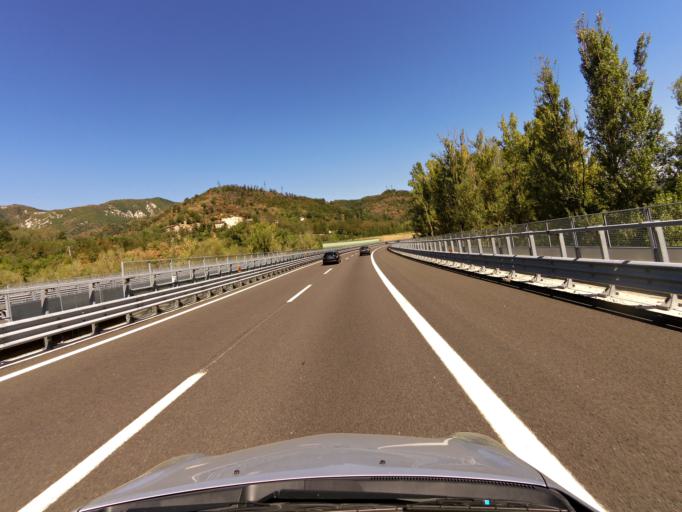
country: IT
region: Emilia-Romagna
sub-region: Provincia di Bologna
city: Grizzana
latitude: 44.2635
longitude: 11.1875
